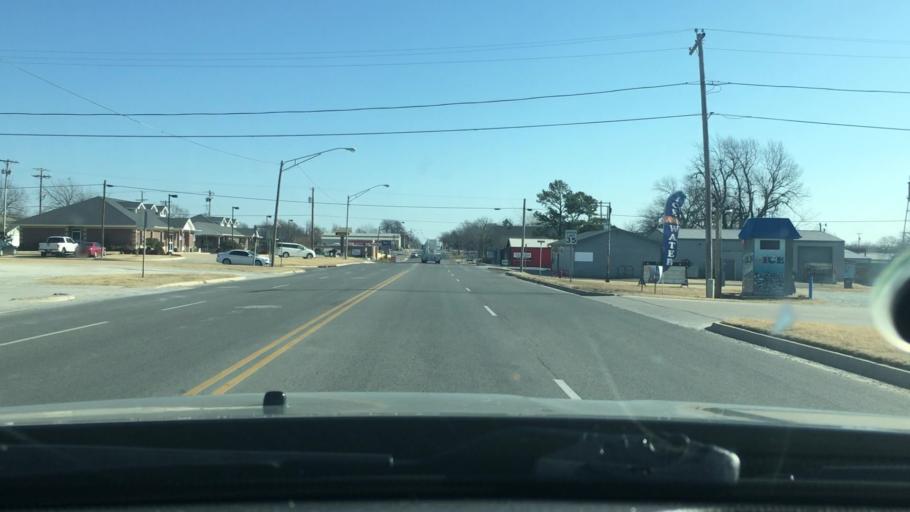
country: US
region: Oklahoma
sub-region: Garvin County
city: Stratford
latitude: 34.7966
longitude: -96.9668
